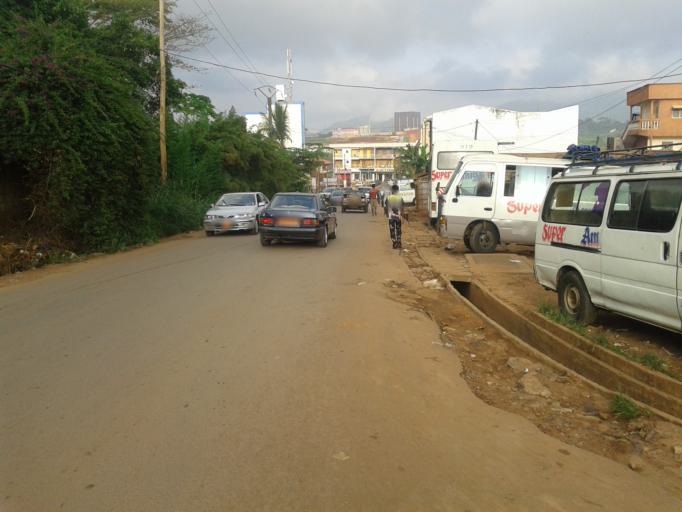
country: CM
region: Centre
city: Yaounde
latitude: 3.9074
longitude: 11.5267
